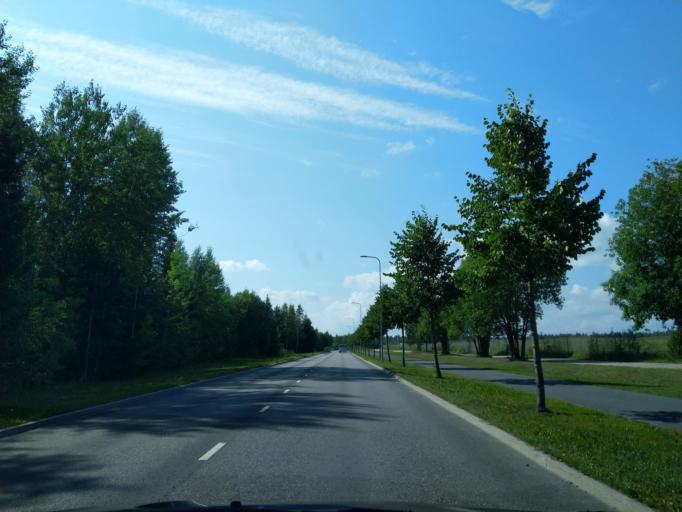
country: FI
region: South Karelia
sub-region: Lappeenranta
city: Lappeenranta
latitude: 61.0375
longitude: 28.1219
